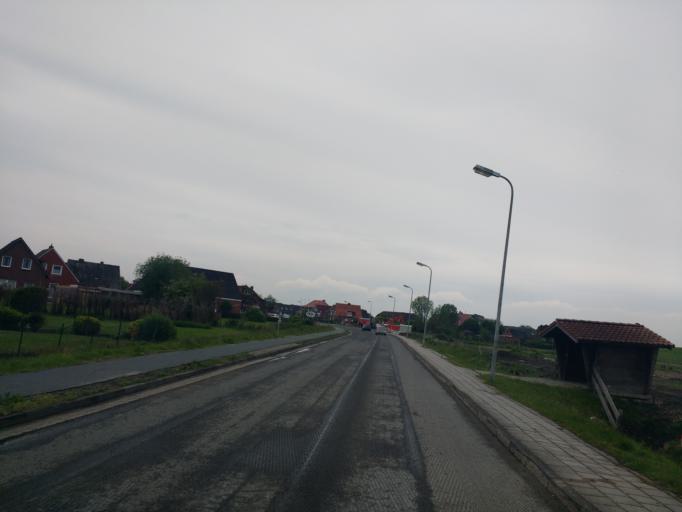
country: DE
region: Lower Saxony
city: Neuharlingersiel
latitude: 53.6996
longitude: 7.6974
